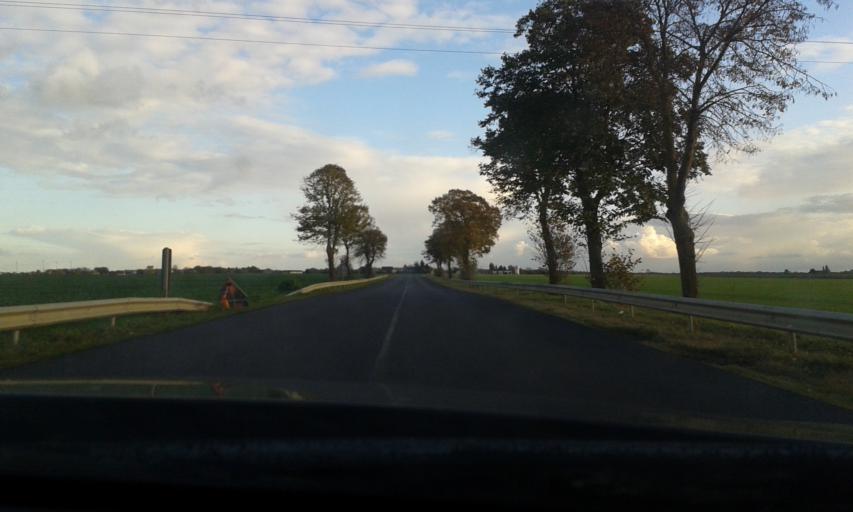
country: FR
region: Centre
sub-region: Departement d'Eure-et-Loir
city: Le Coudray
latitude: 48.4234
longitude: 1.5222
